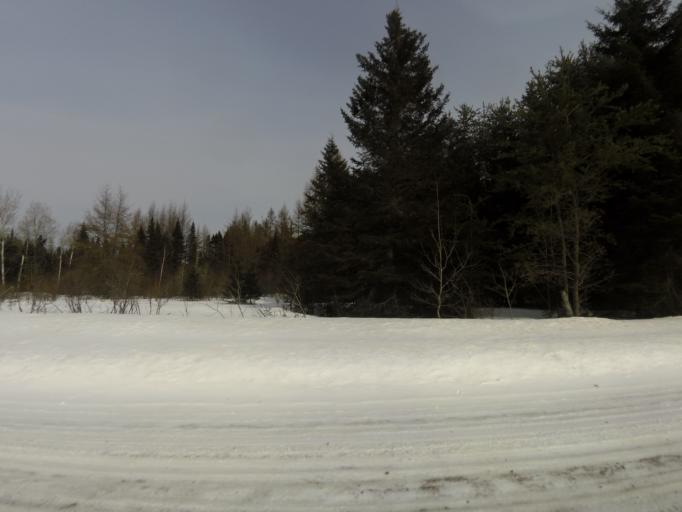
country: CA
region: Quebec
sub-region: Laurentides
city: Ferme-Neuve
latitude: 46.8335
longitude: -75.3164
